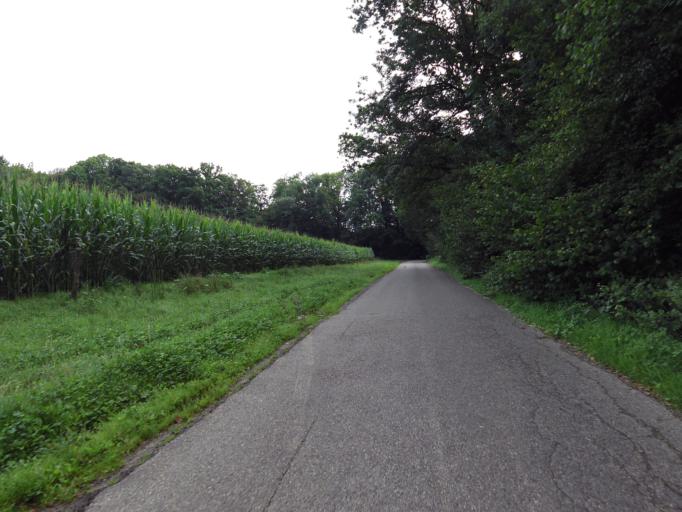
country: NL
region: Limburg
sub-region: Gemeente Nuth
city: Nuth
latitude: 50.9020
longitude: 5.8768
